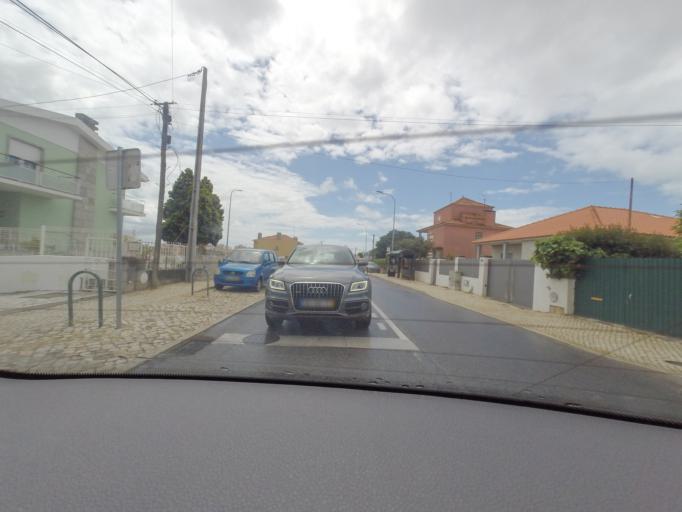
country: PT
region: Lisbon
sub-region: Cascais
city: Sao Domingos de Rana
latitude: 38.6990
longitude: -9.3413
